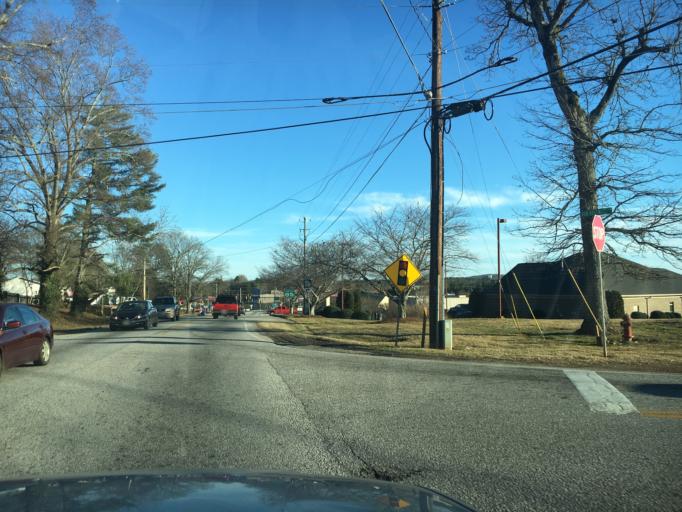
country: US
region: Georgia
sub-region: Habersham County
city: Demorest
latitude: 34.5459
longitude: -83.5484
